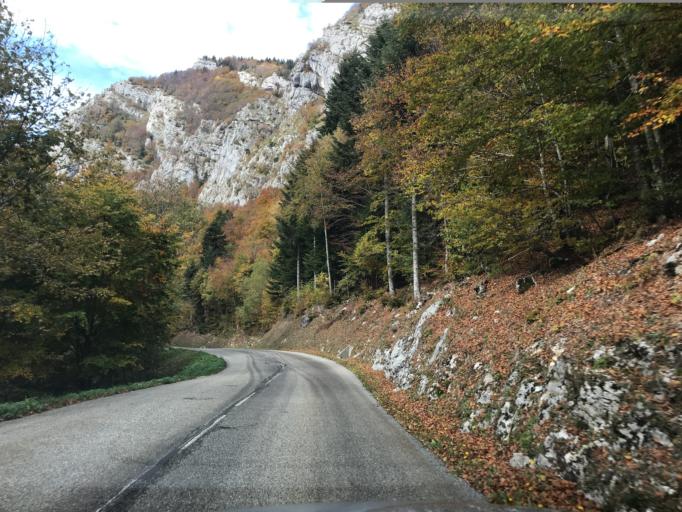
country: FR
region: Rhone-Alpes
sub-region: Departement de la Savoie
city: Vimines
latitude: 45.4538
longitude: 5.8527
